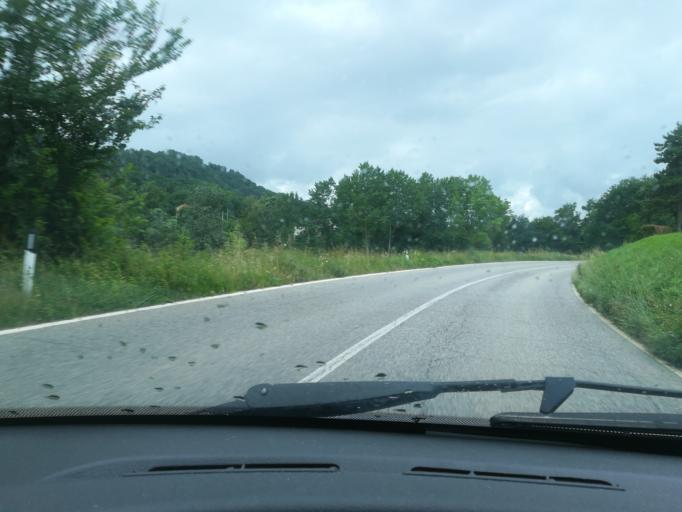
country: IT
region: The Marches
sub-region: Provincia di Macerata
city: San Ginesio
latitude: 43.0980
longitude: 13.3370
